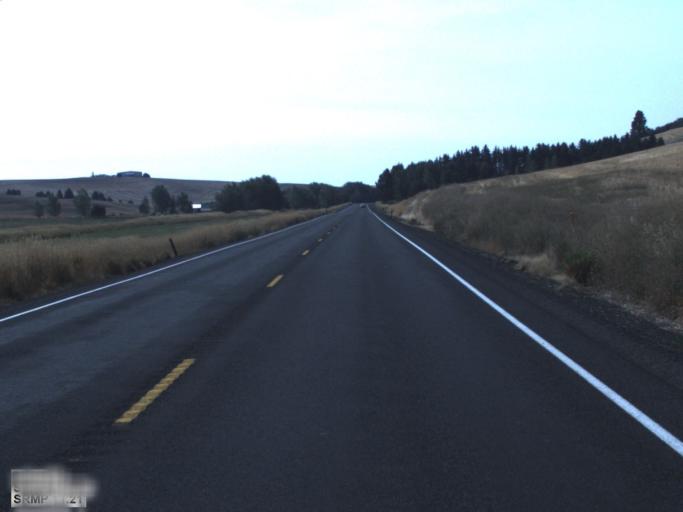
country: US
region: Washington
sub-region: Whitman County
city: Pullman
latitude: 46.8733
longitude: -117.1271
